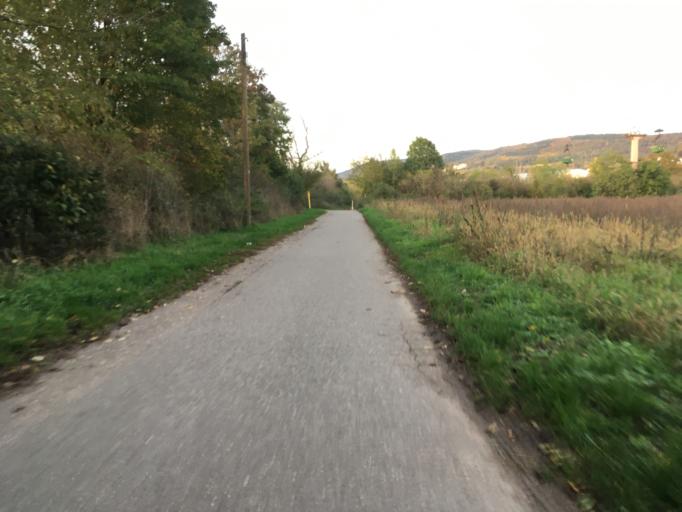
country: DE
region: Baden-Wuerttemberg
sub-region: Karlsruhe Region
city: Leimen
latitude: 49.3380
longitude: 8.6831
